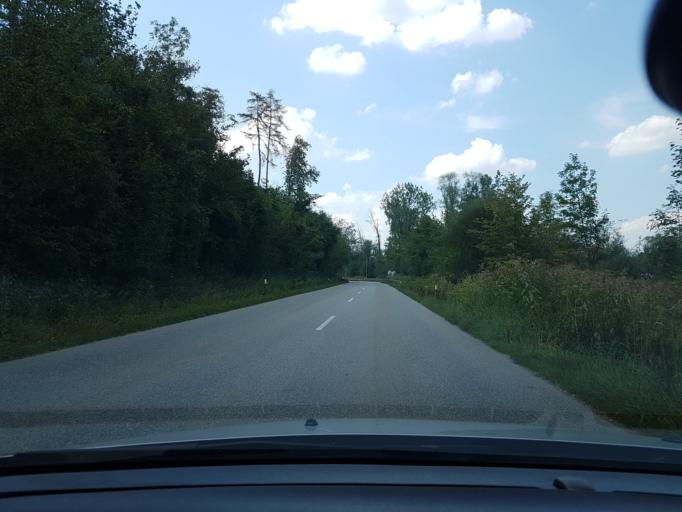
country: DE
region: Bavaria
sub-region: Upper Bavaria
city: Altoetting
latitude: 48.2422
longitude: 12.6694
